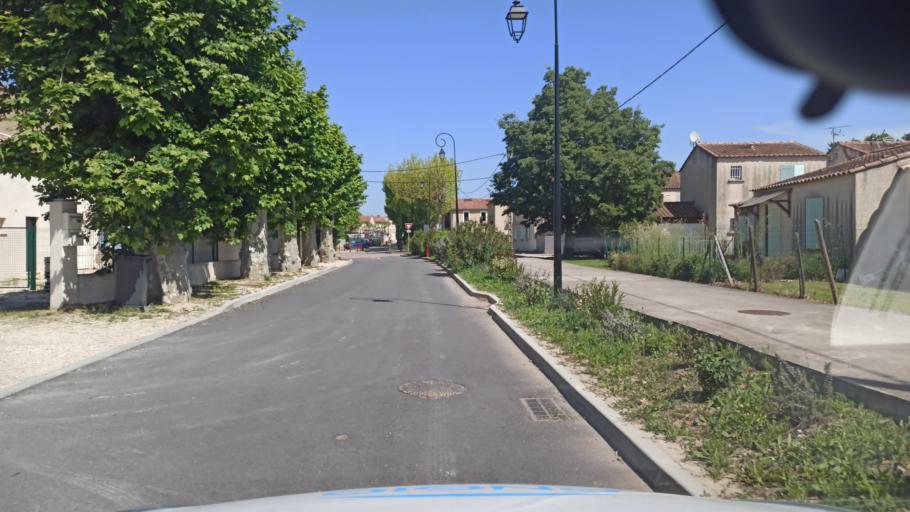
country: FR
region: Provence-Alpes-Cote d'Azur
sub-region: Departement des Bouches-du-Rhone
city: Saint-Andiol
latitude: 43.8314
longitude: 4.9038
